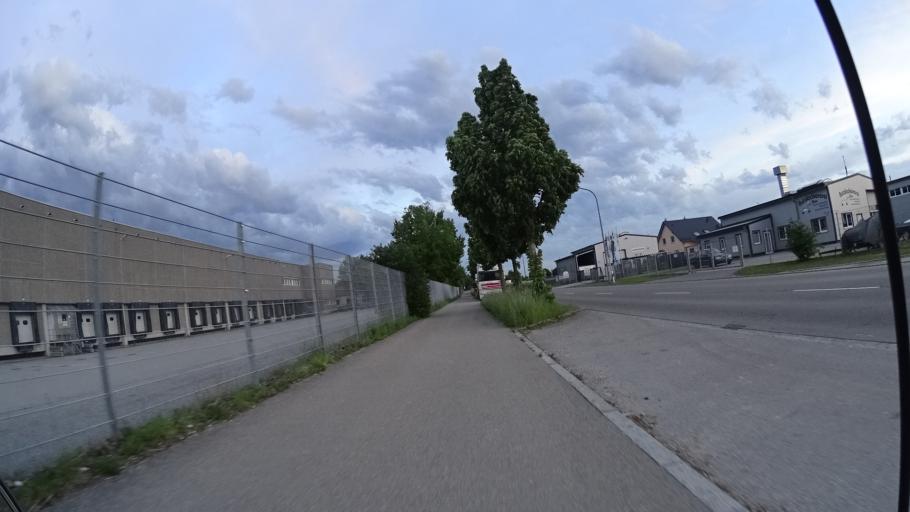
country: DE
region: Bavaria
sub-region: Swabia
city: Pfaffenhofen an der Roth
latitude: 48.3574
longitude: 10.1502
